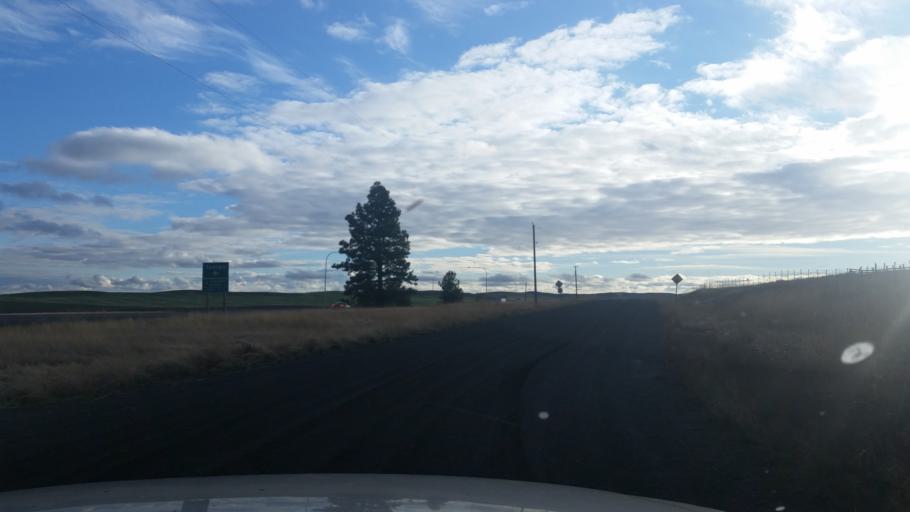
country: US
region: Washington
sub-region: Spokane County
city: Cheney
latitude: 47.4272
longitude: -117.3895
